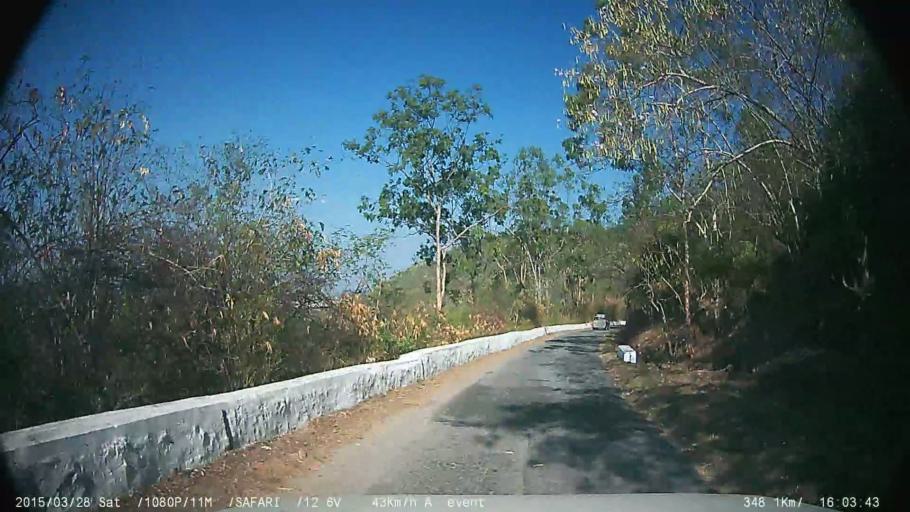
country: IN
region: Karnataka
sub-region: Mysore
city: Mysore
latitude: 12.2815
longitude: 76.6712
